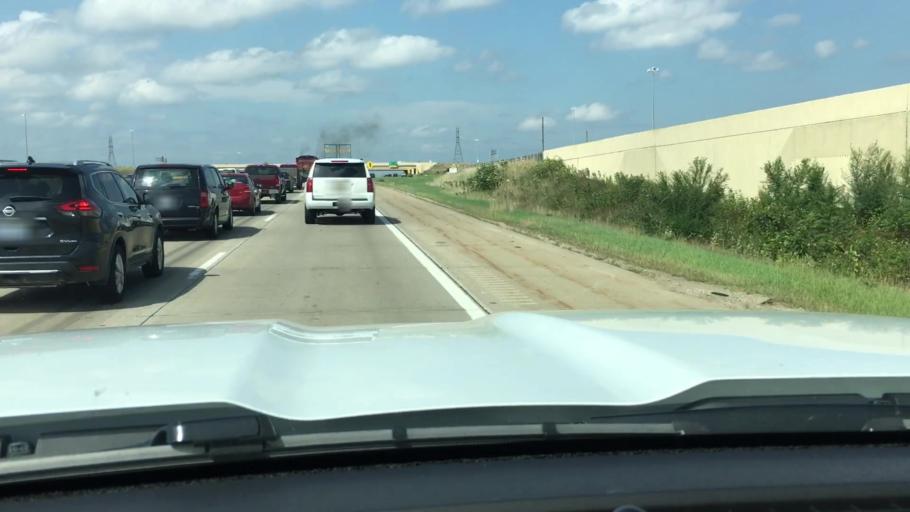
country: US
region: Michigan
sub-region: Kent County
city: Cutlerville
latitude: 42.8437
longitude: -85.6782
